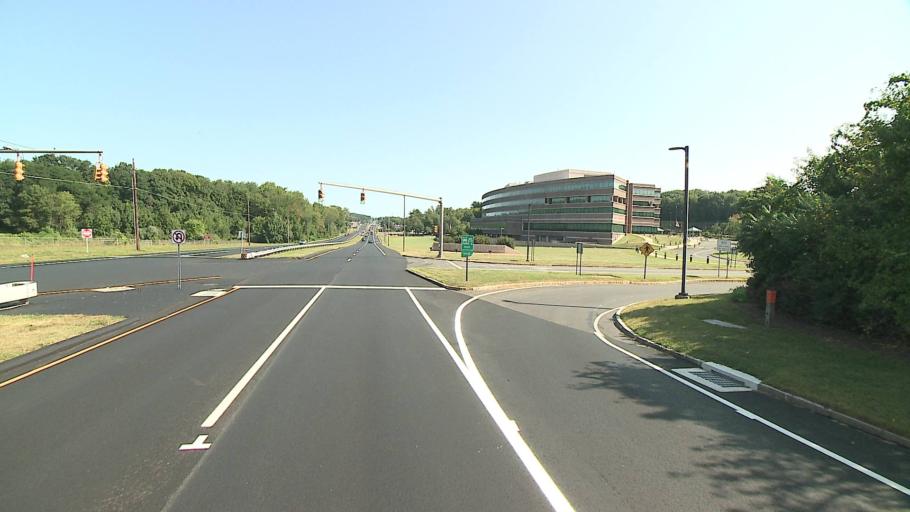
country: US
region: Connecticut
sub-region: Hartford County
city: Newington
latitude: 41.6719
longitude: -72.7165
